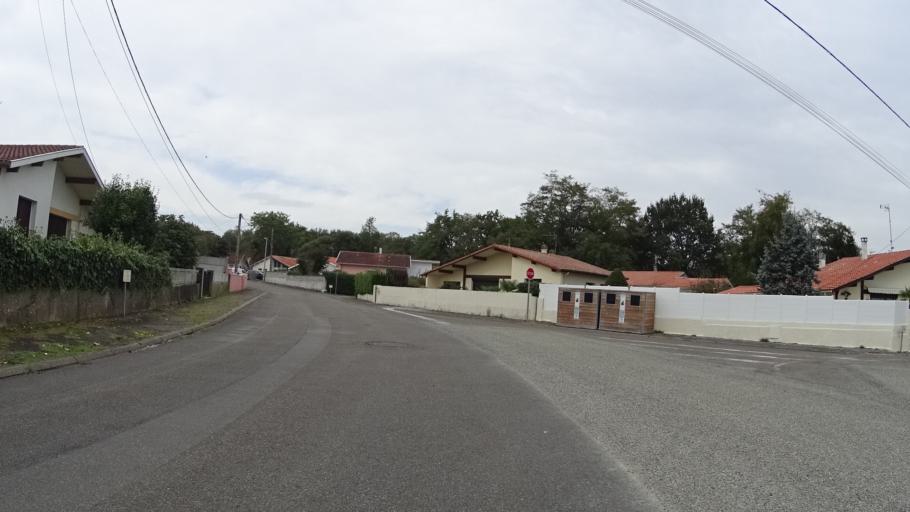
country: FR
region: Aquitaine
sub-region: Departement des Landes
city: Saint-Paul-les-Dax
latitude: 43.7299
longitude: -1.0730
